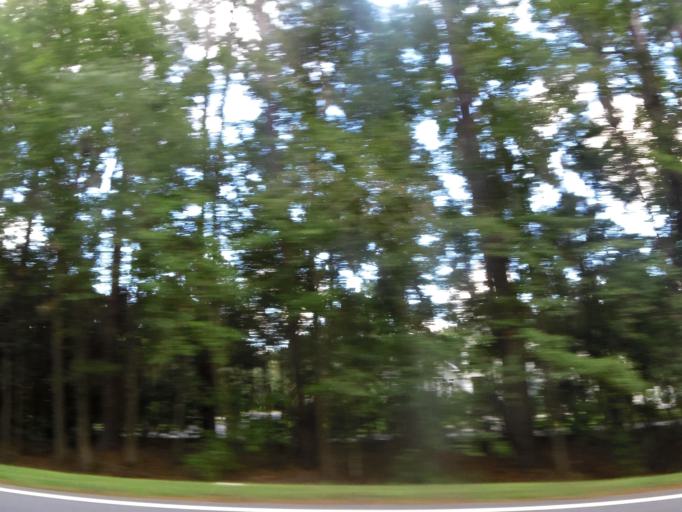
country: US
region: Georgia
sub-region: Glynn County
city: Saint Simon Mills
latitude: 31.1707
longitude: -81.4024
